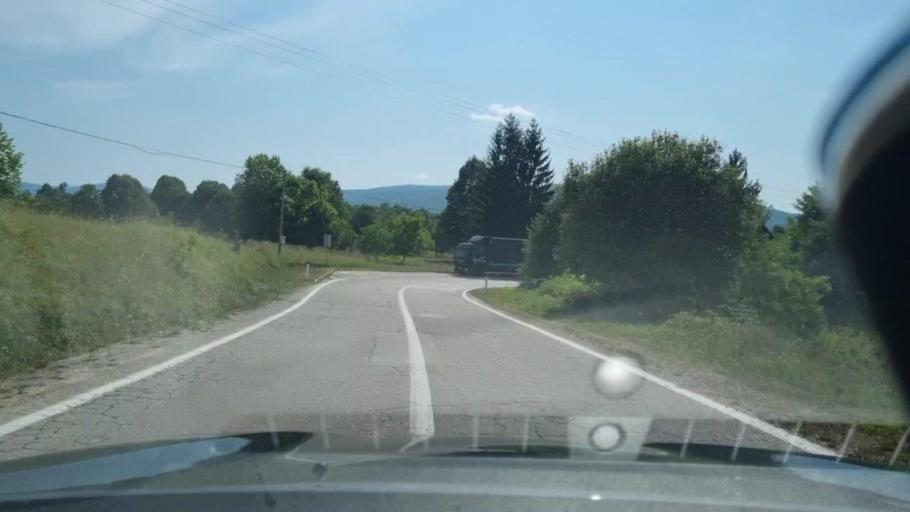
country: BA
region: Federation of Bosnia and Herzegovina
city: Bosanska Krupa
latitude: 44.8306
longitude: 16.1715
